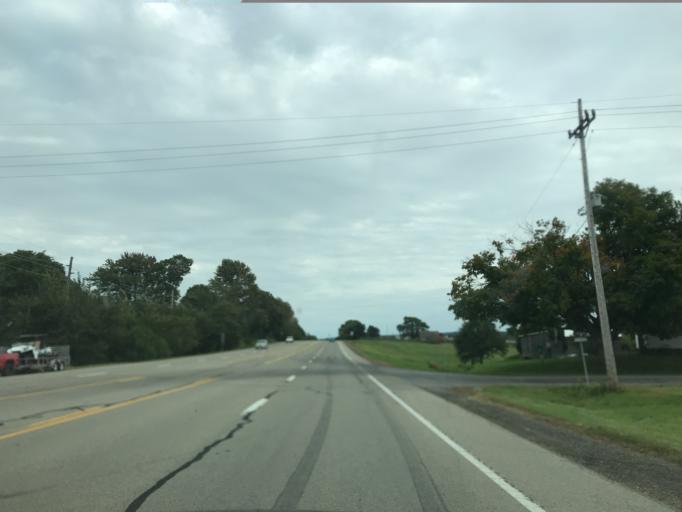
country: US
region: Pennsylvania
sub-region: Erie County
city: North East
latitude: 42.2278
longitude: -79.7964
